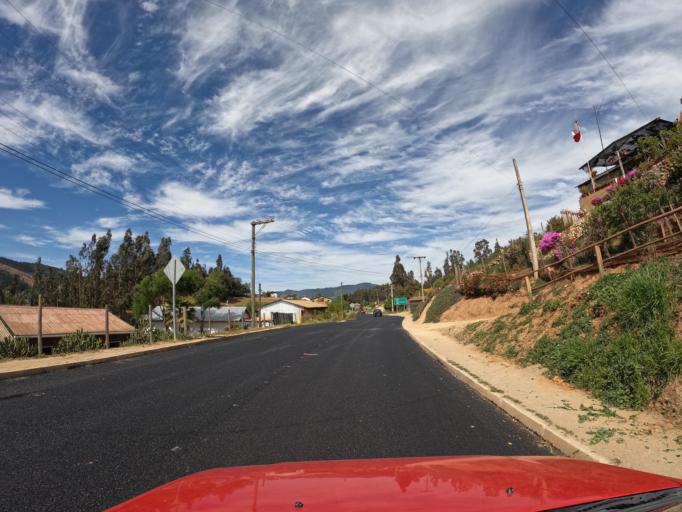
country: CL
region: Maule
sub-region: Provincia de Talca
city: Constitucion
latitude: -35.0975
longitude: -72.0110
